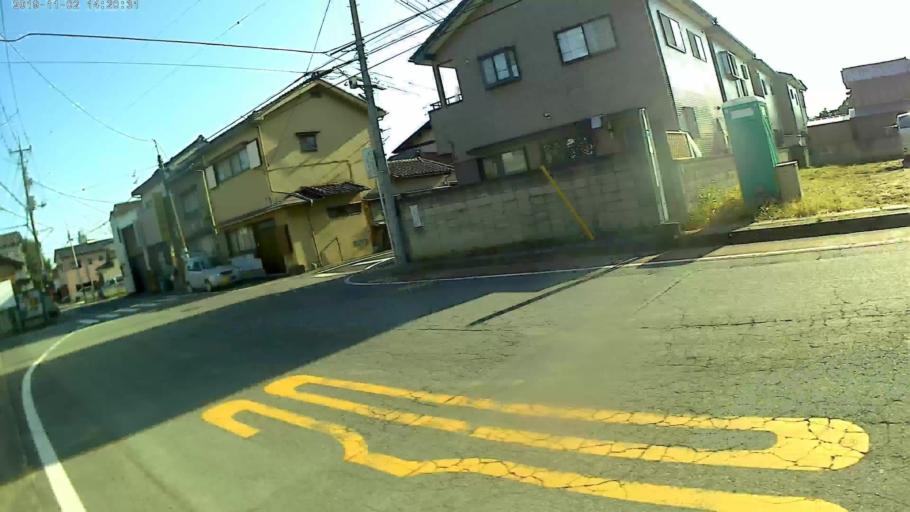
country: JP
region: Gunma
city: Takasaki
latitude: 36.3323
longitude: 138.9935
